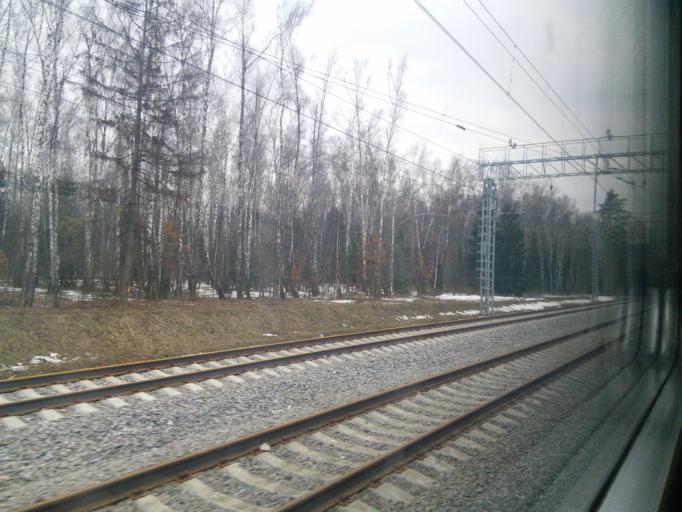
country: RU
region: Moskovskaya
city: Vostryakovo
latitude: 55.4277
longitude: 37.8435
